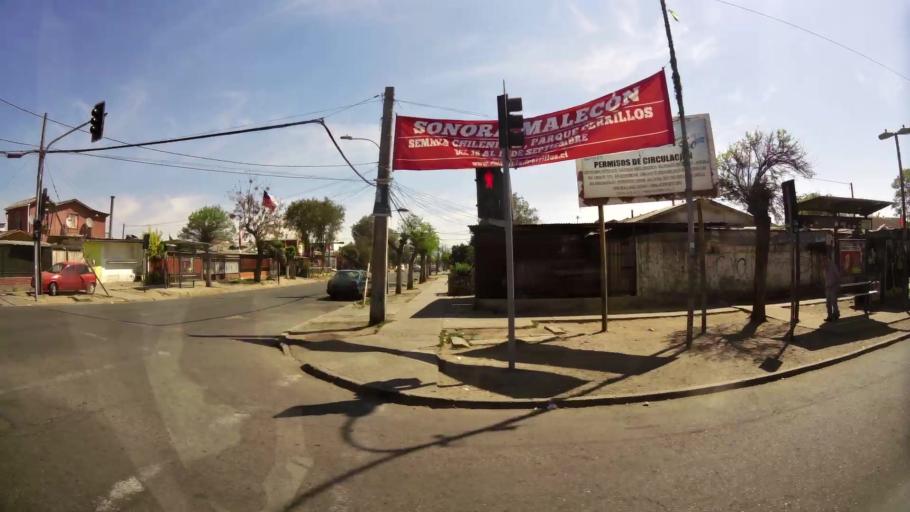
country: CL
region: Santiago Metropolitan
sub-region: Provincia de Santiago
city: Lo Prado
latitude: -33.5022
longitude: -70.7291
